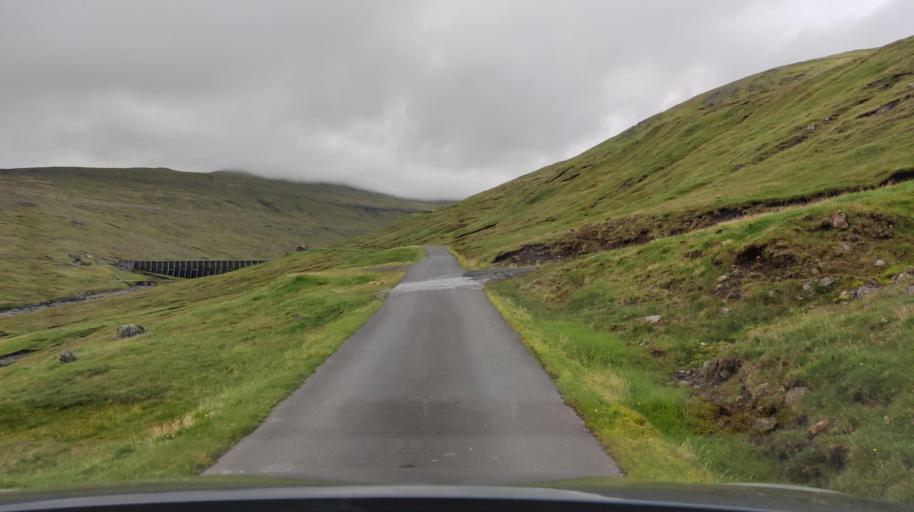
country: FO
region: Streymoy
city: Vestmanna
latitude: 62.1728
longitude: -7.1472
